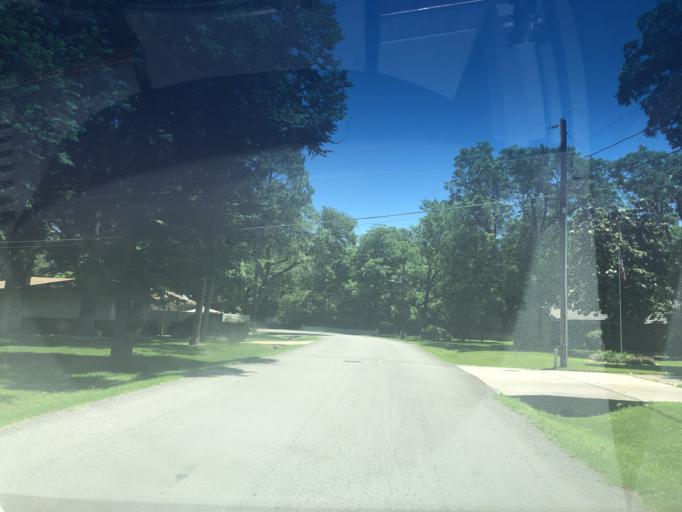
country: US
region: Texas
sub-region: Dallas County
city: Grand Prairie
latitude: 32.7738
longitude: -97.0343
